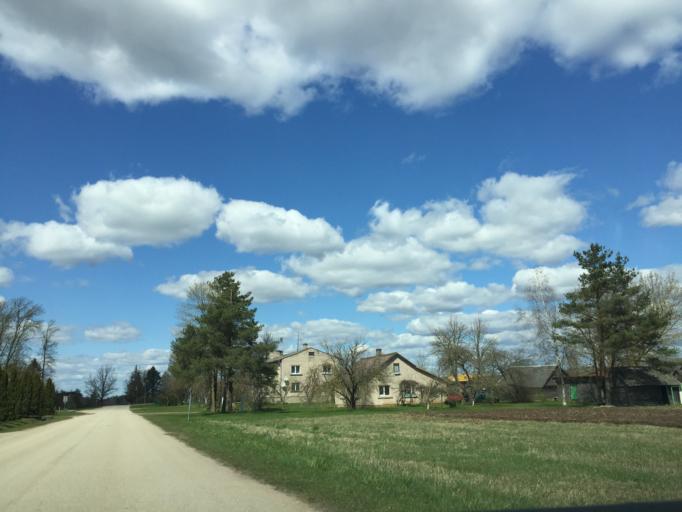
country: LV
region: Rezekne
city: Rezekne
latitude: 56.5620
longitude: 27.1431
